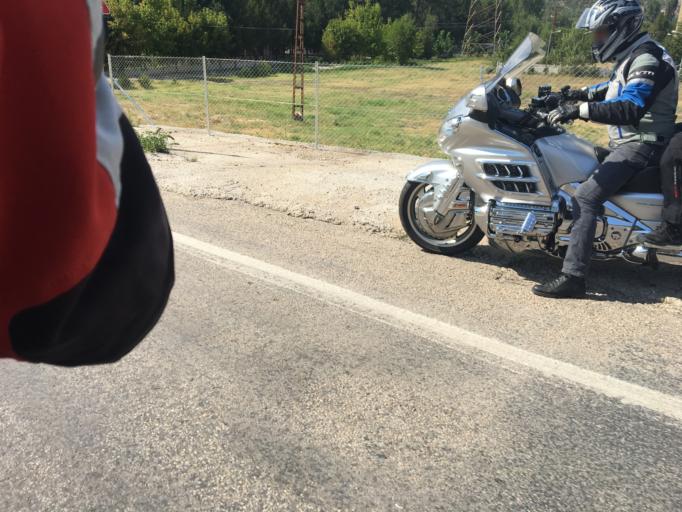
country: TR
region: Ankara
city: Nallihan
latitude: 40.1776
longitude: 31.3441
